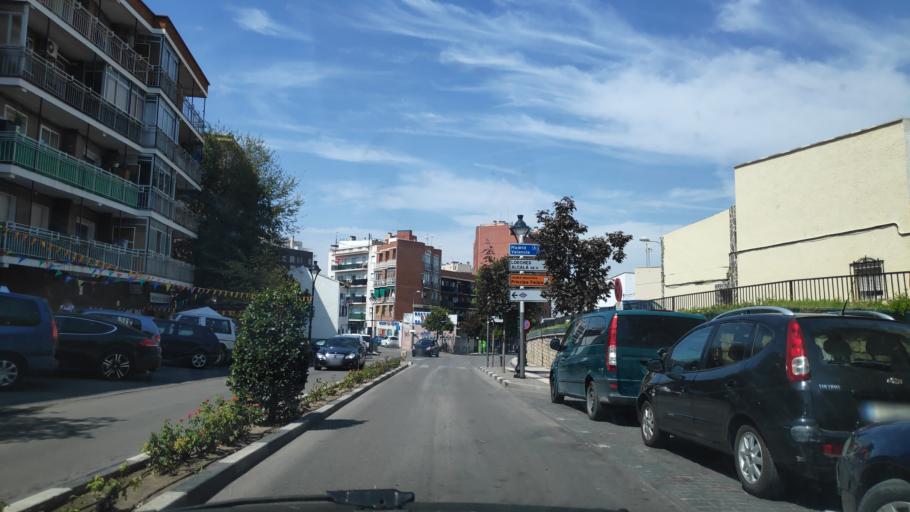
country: ES
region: Madrid
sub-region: Provincia de Madrid
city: Arganda
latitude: 40.3035
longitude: -3.4437
